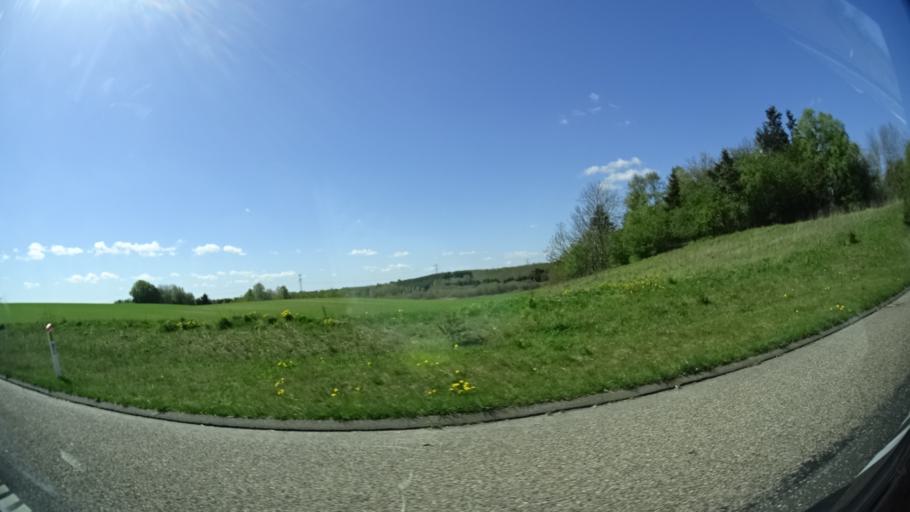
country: DK
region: Central Jutland
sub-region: Arhus Kommune
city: Trige
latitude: 56.3166
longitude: 10.1190
